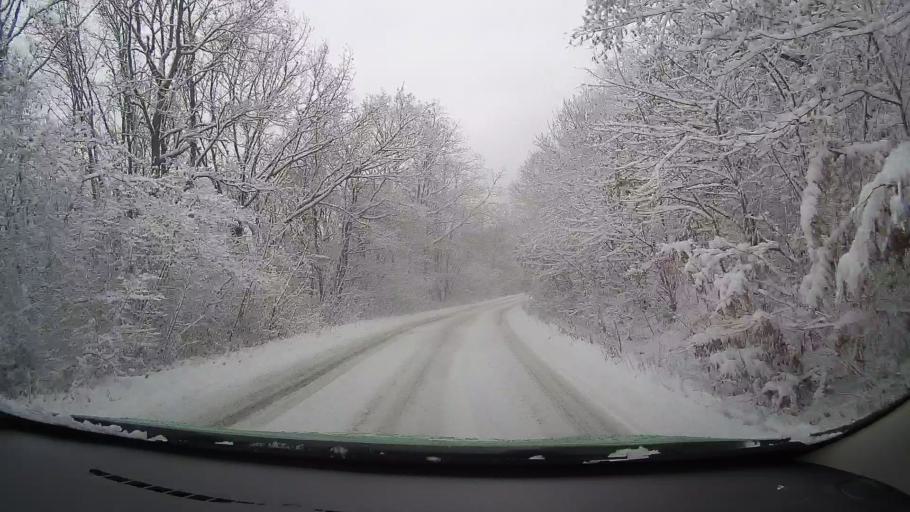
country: RO
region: Hunedoara
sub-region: Municipiul Deva
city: Deva
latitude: 45.8571
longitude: 22.8810
